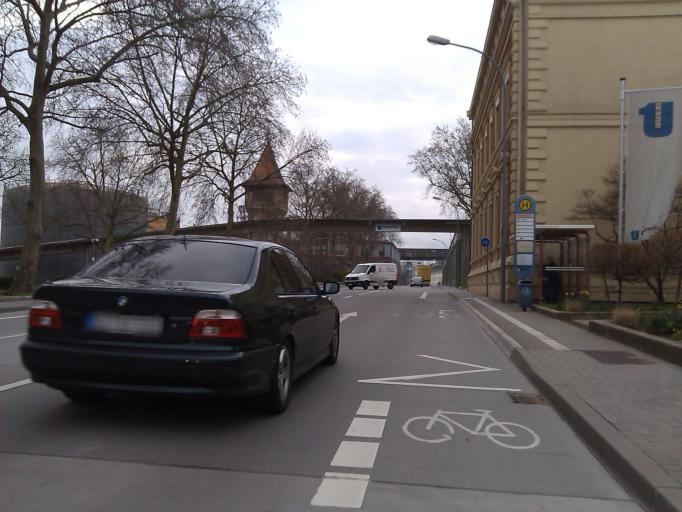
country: DE
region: Rheinland-Pfalz
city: Mainz
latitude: 50.0299
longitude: 8.2543
